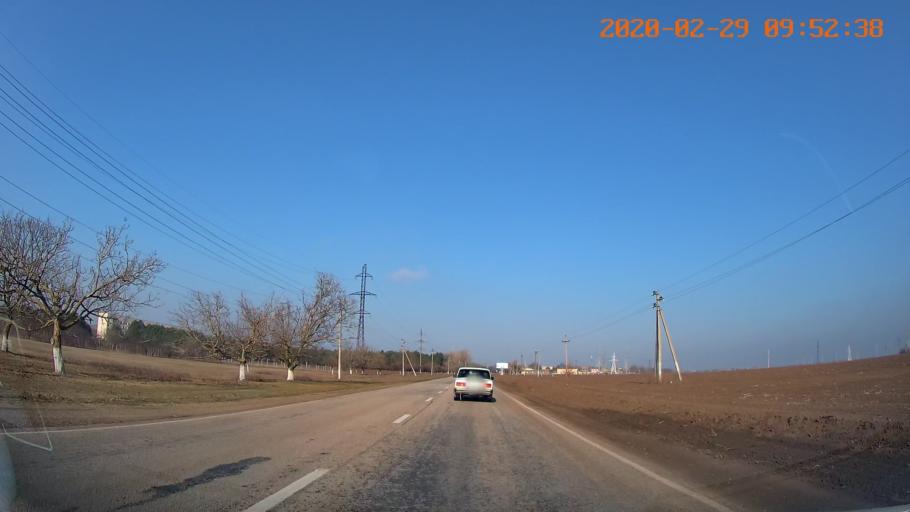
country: MD
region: Telenesti
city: Slobozia
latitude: 46.7171
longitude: 29.7287
